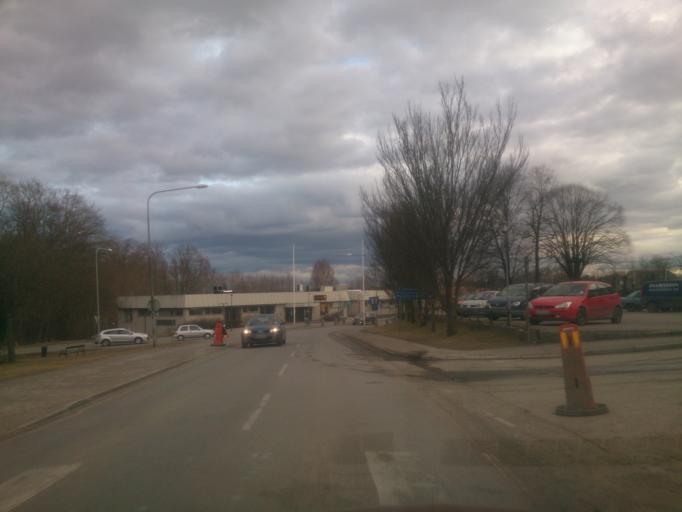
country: SE
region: OEstergoetland
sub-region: Norrkopings Kommun
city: Jursla
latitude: 58.6664
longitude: 16.1813
